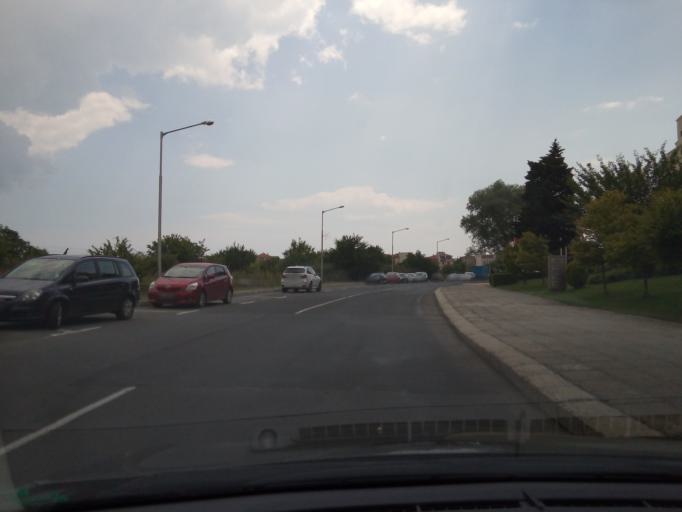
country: BG
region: Burgas
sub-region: Obshtina Nesebur
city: Ravda
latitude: 42.6541
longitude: 27.6988
